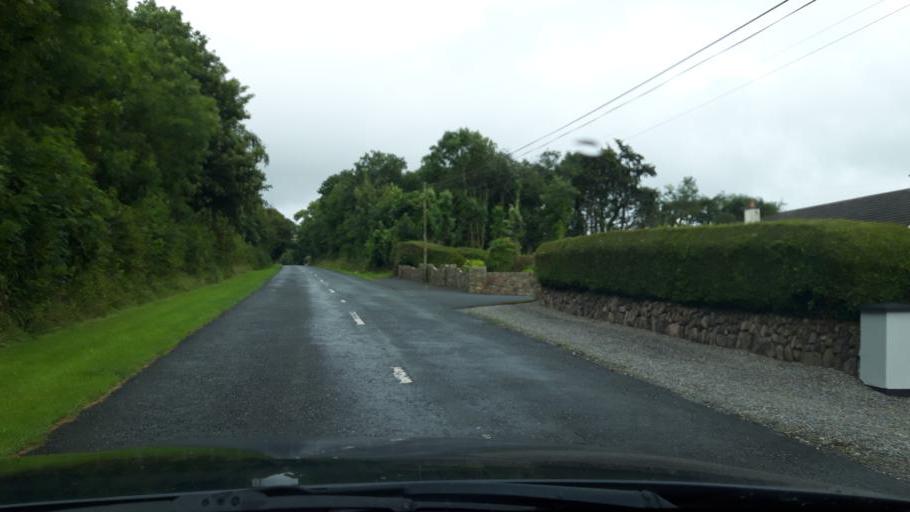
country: IE
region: Munster
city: Cahir
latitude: 52.1781
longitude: -7.8498
